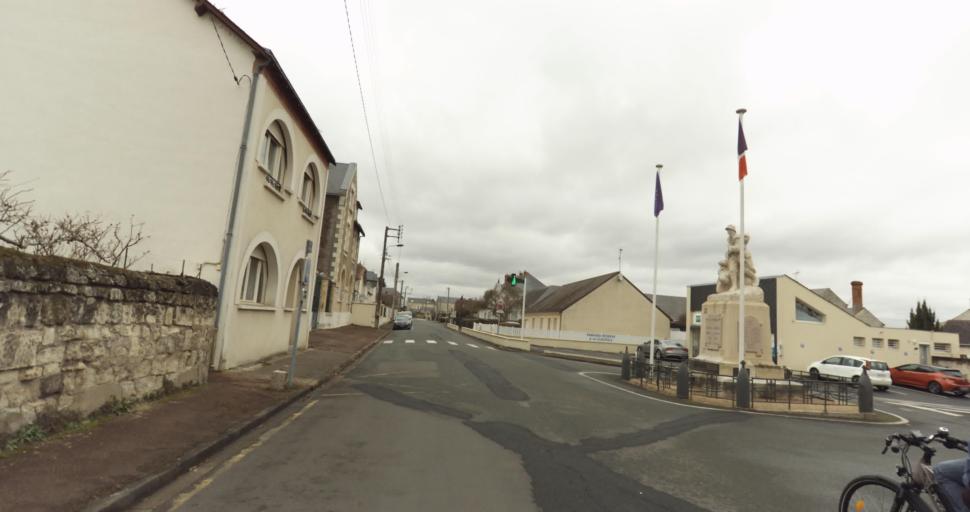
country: FR
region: Pays de la Loire
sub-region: Departement de Maine-et-Loire
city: Saumur
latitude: 47.2433
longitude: -0.0943
